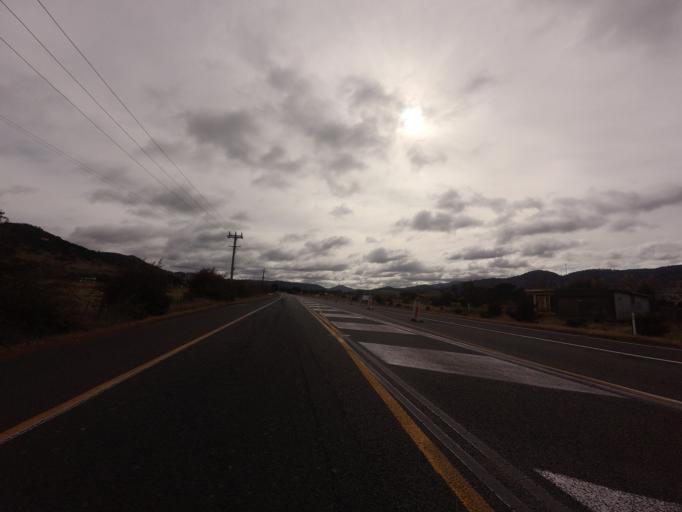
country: AU
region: Tasmania
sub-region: Brighton
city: Bridgewater
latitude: -42.6575
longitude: 147.2442
